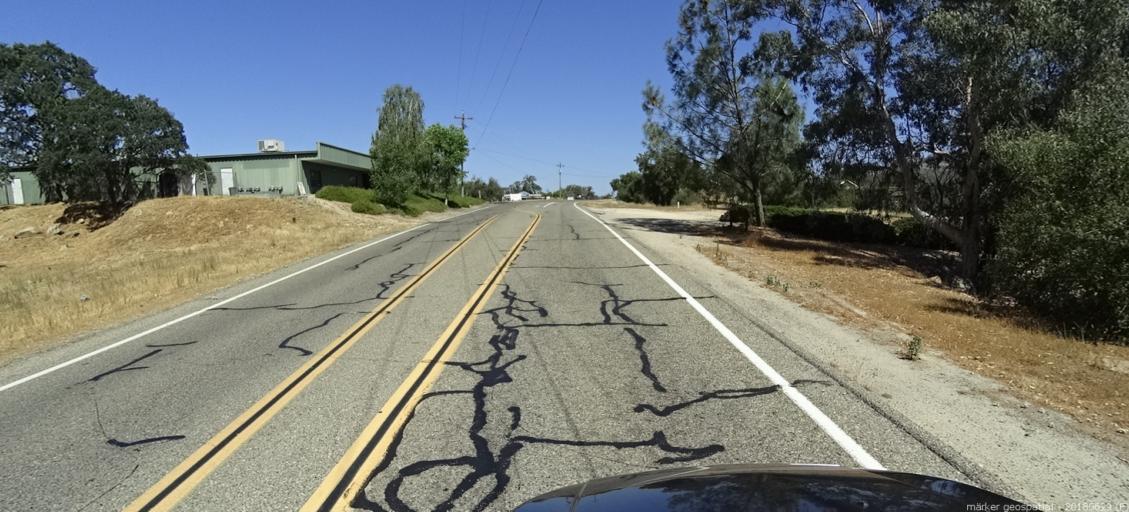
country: US
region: California
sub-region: Madera County
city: Yosemite Lakes
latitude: 37.1609
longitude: -119.7474
